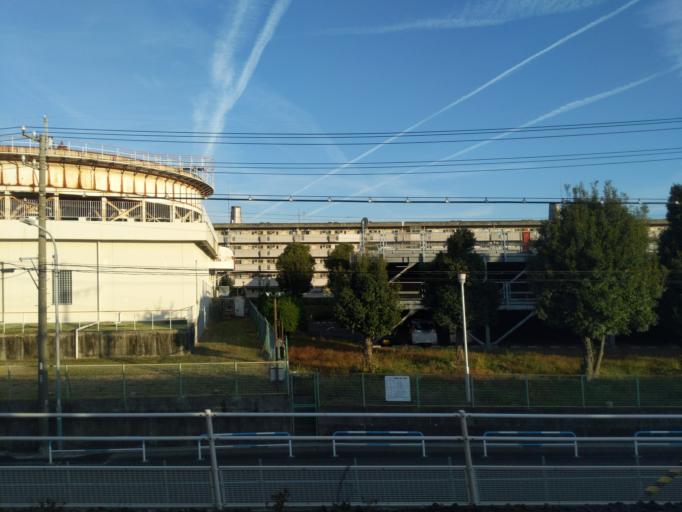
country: JP
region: Aichi
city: Kasugai
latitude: 35.2128
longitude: 136.9536
